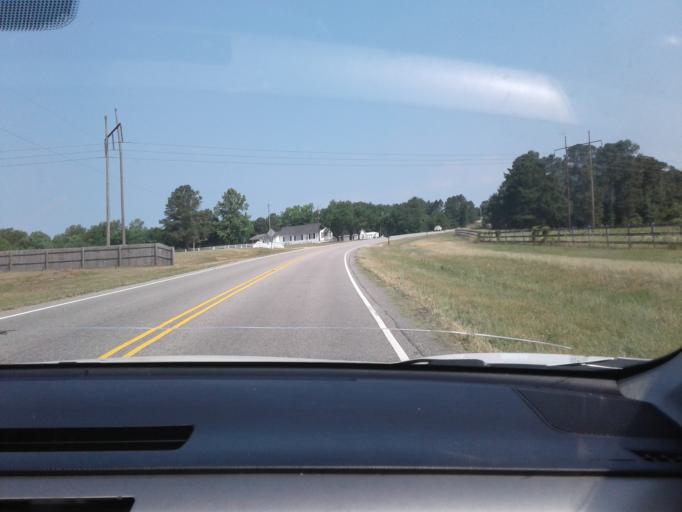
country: US
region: North Carolina
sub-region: Harnett County
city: Coats
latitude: 35.4539
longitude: -78.6887
